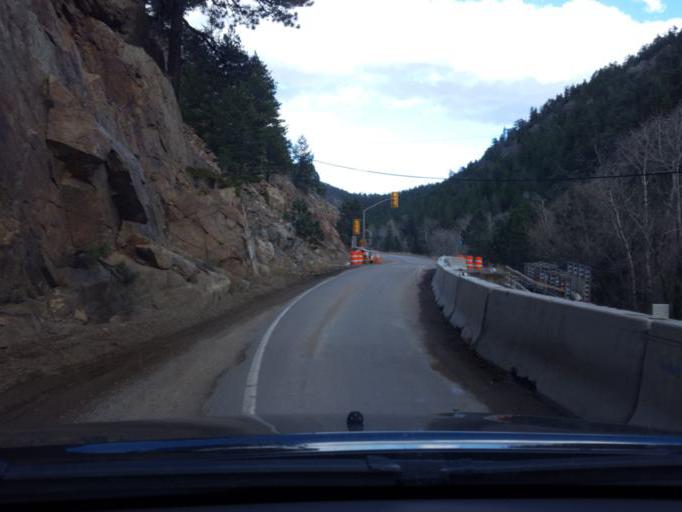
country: US
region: Colorado
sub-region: Boulder County
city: Boulder
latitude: 40.1086
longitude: -105.3721
